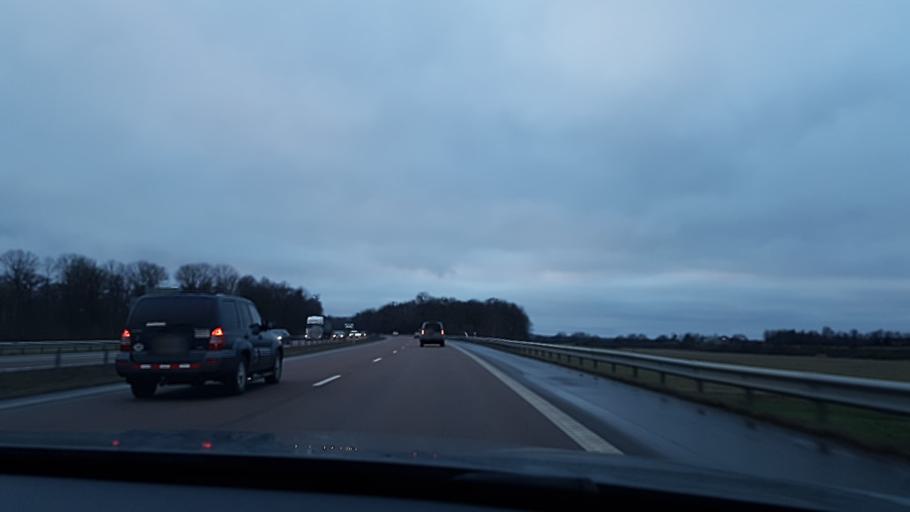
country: SE
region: Skane
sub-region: Helsingborg
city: Hyllinge
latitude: 56.0979
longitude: 12.8318
